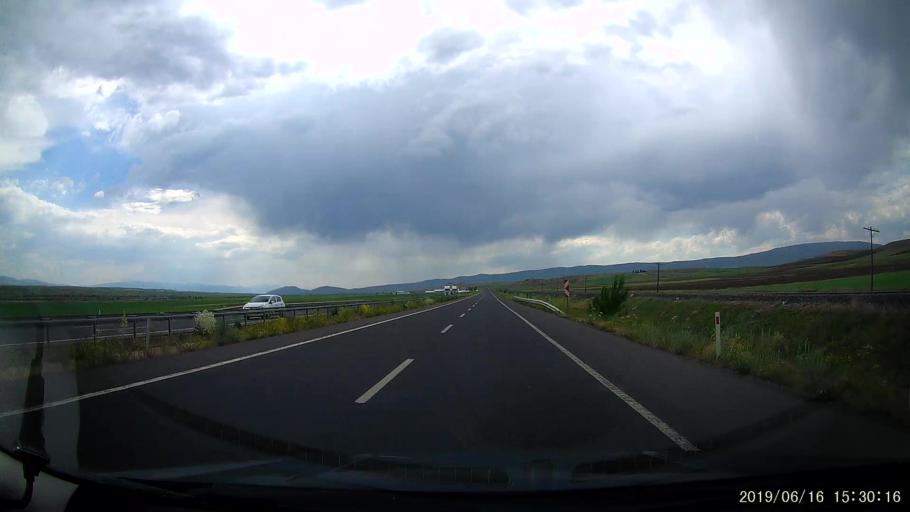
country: TR
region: Erzurum
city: Horasan
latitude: 40.0334
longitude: 42.1102
